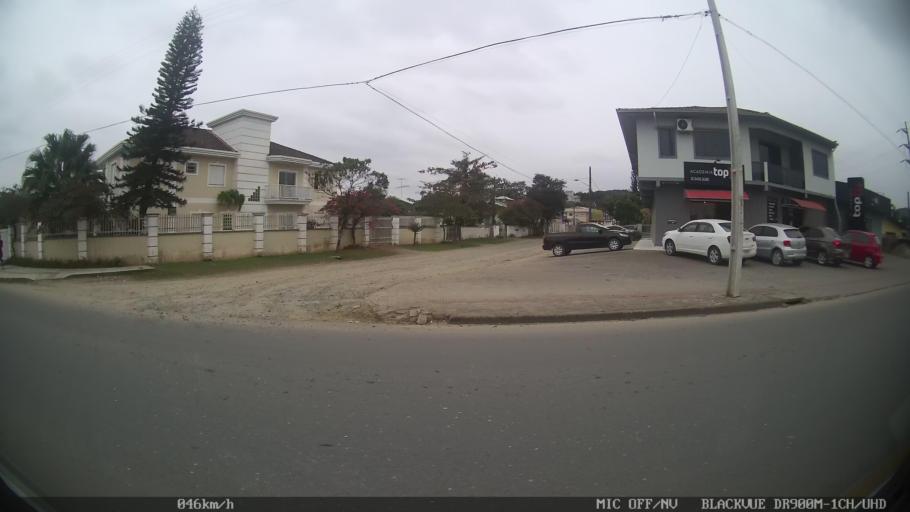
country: BR
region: Santa Catarina
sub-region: Joinville
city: Joinville
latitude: -26.3671
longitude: -48.8292
